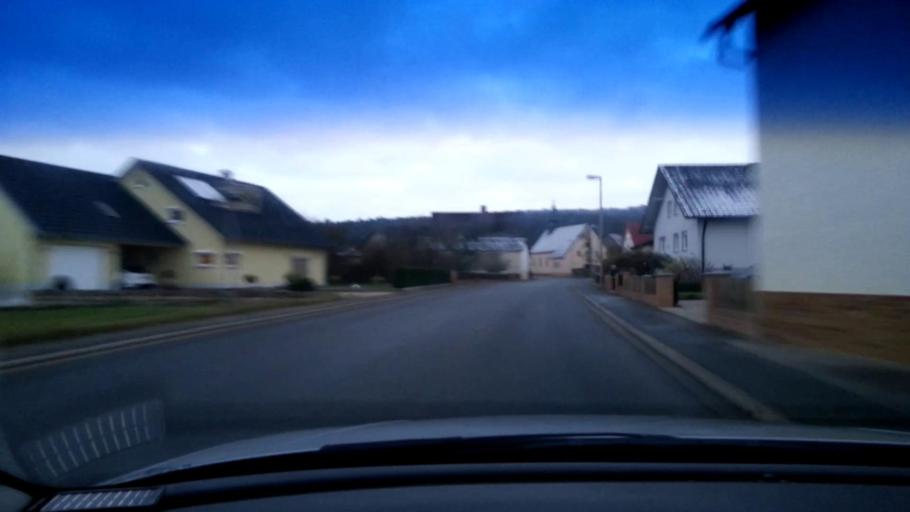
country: DE
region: Bavaria
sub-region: Upper Franconia
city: Pettstadt
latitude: 49.8482
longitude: 10.8931
